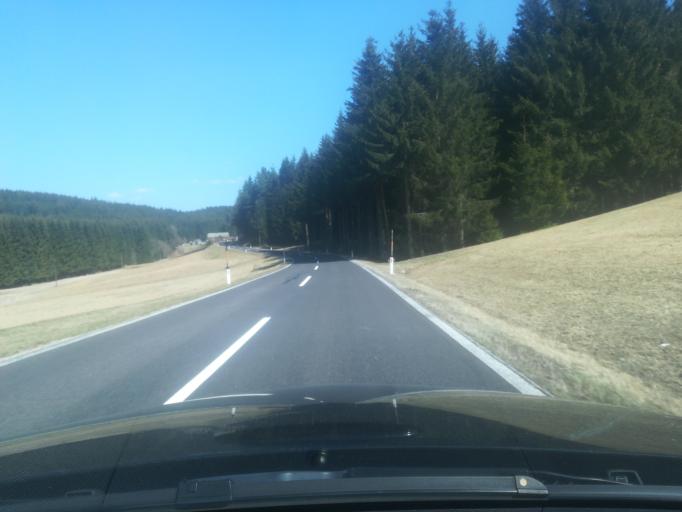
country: AT
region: Lower Austria
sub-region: Politischer Bezirk Zwettl
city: Langschlag
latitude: 48.4965
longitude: 14.8221
